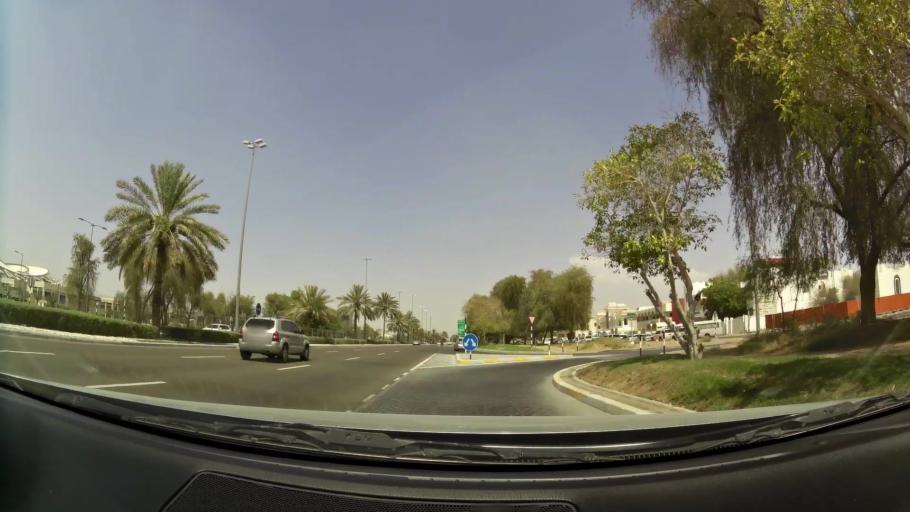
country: AE
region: Abu Dhabi
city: Al Ain
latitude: 24.2423
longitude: 55.7160
